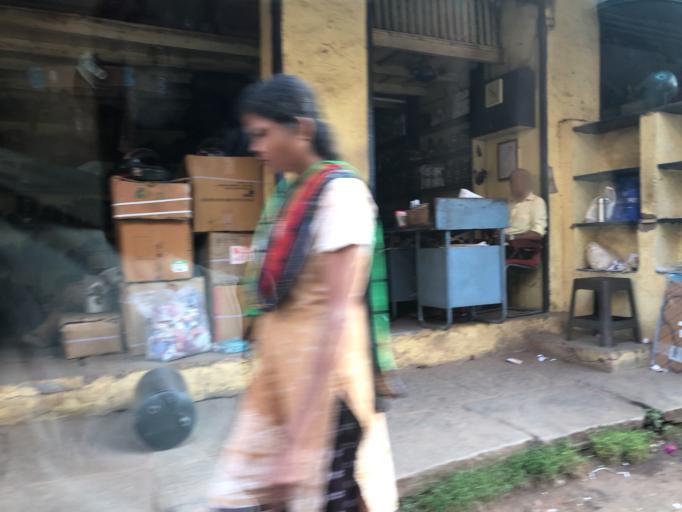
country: IN
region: Karnataka
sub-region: Dakshina Kannada
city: Mangalore
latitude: 12.8657
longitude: 74.8364
